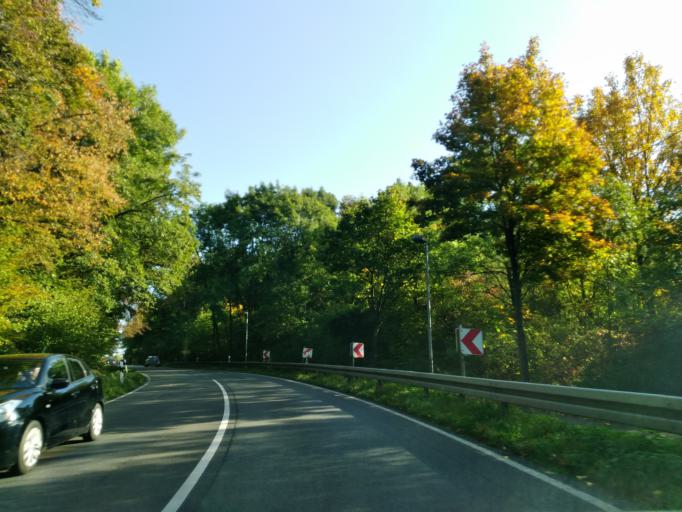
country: DE
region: North Rhine-Westphalia
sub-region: Regierungsbezirk Koln
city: Hennef
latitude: 50.7437
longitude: 7.3481
